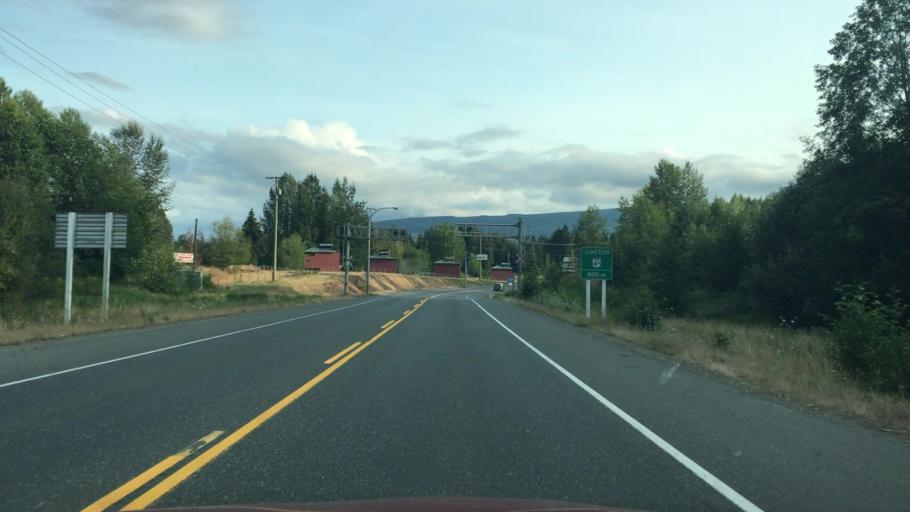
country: CA
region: British Columbia
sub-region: Regional District of Nanaimo
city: Parksville
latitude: 49.3072
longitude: -124.4501
